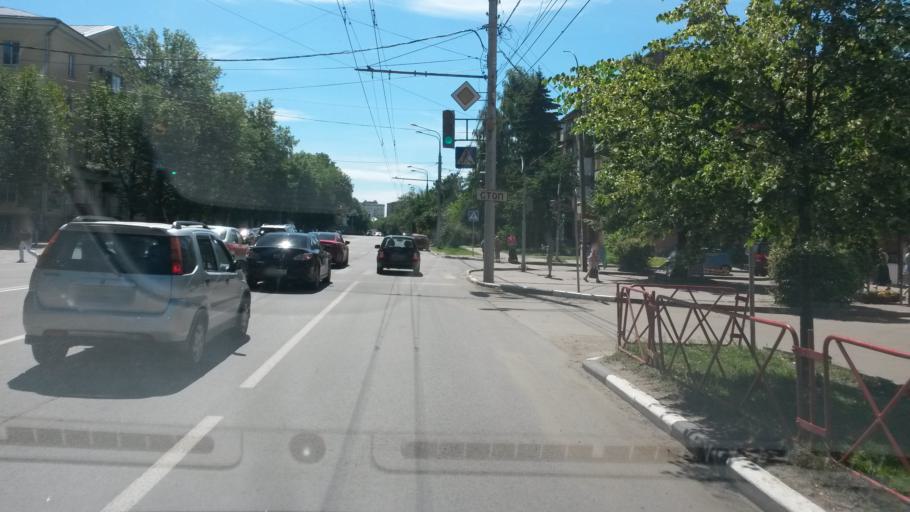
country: RU
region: Jaroslavl
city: Yaroslavl
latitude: 57.6300
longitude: 39.8587
